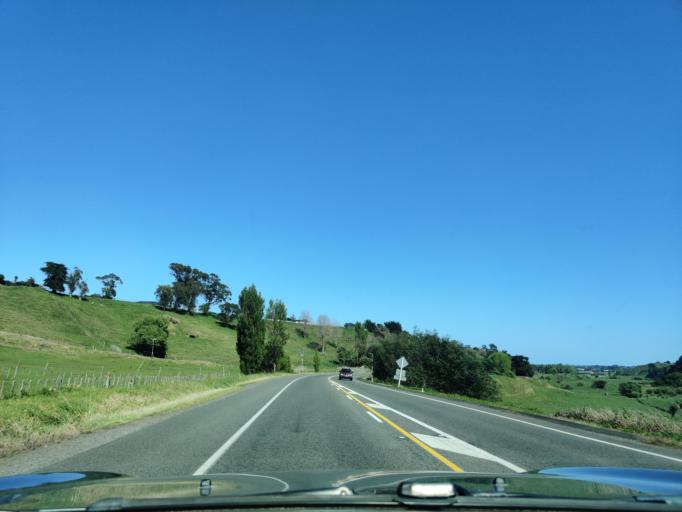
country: NZ
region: Manawatu-Wanganui
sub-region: Wanganui District
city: Wanganui
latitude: -39.9577
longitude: 175.0789
